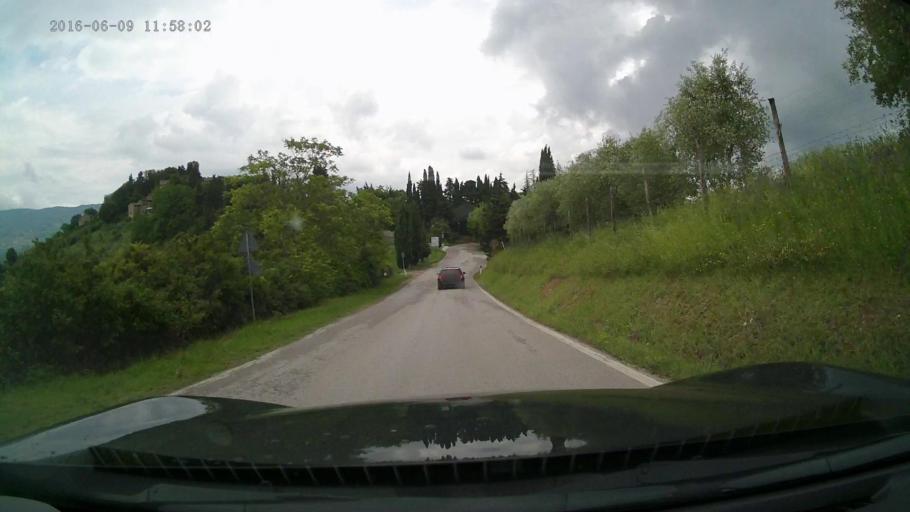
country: IT
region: Tuscany
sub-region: Province of Florence
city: Panzano in Chianti
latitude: 43.5492
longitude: 11.3055
